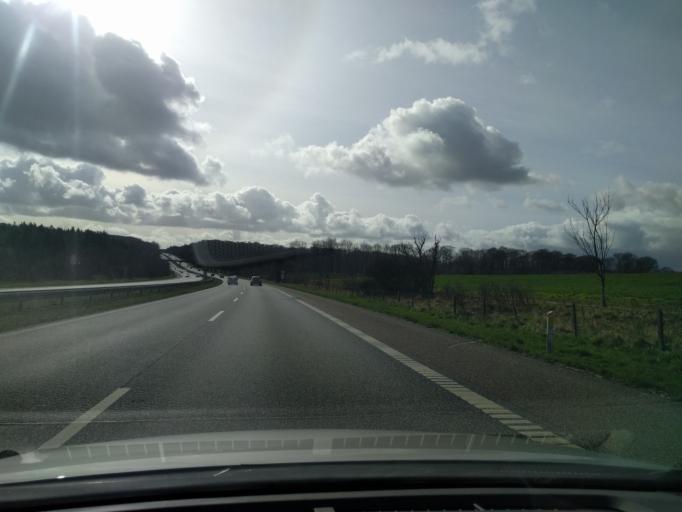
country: DK
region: South Denmark
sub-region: Kolding Kommune
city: Kolding
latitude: 55.5075
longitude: 9.4246
